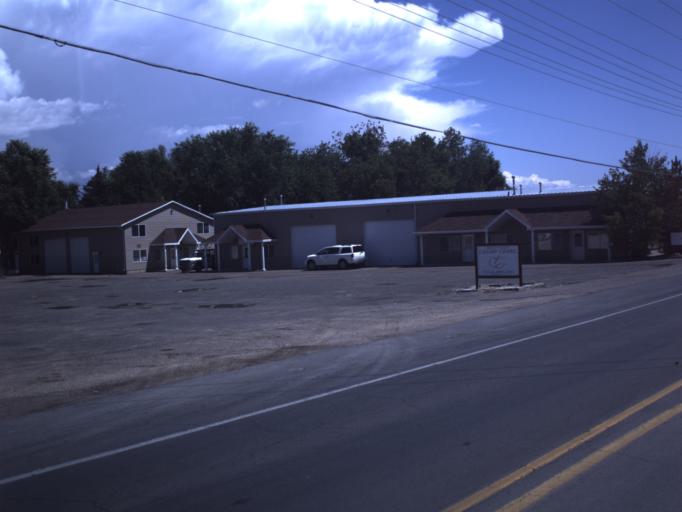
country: US
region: Utah
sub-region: Uintah County
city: Maeser
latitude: 40.4626
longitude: -109.5785
